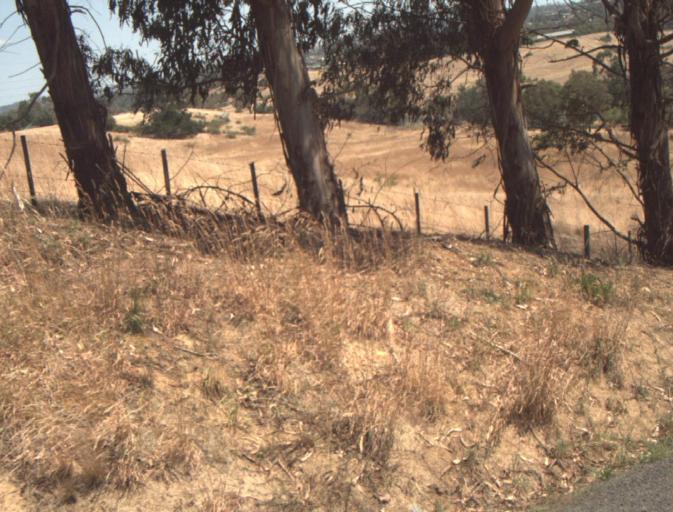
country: AU
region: Tasmania
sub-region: Launceston
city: Newstead
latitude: -41.4709
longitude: 147.1903
